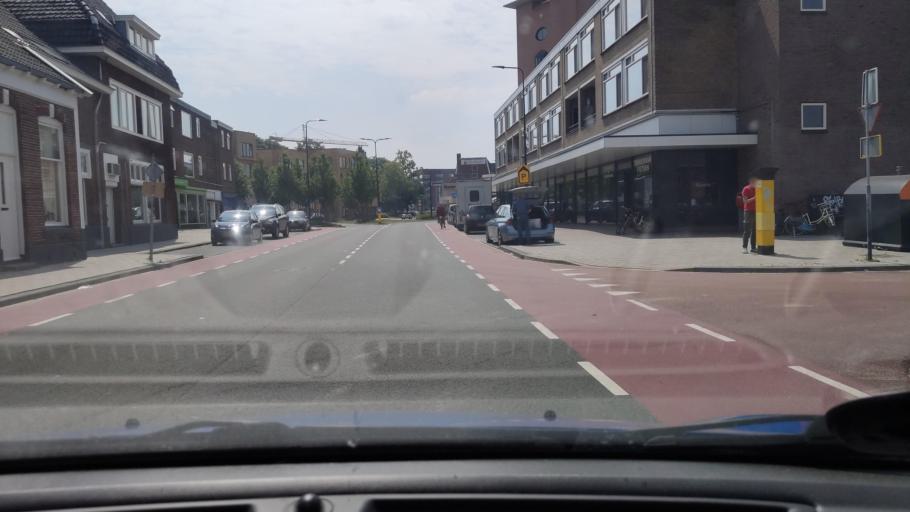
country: NL
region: Overijssel
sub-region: Gemeente Enschede
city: Enschede
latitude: 52.2264
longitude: 6.8909
